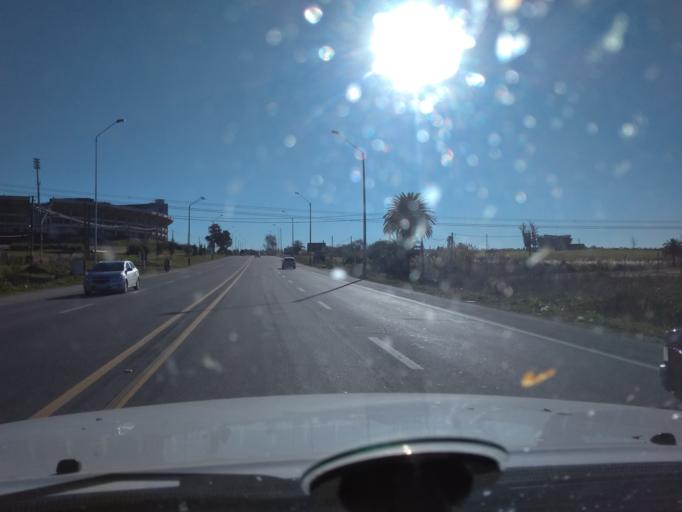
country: UY
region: Canelones
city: Colonia Nicolich
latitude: -34.7976
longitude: -56.0629
